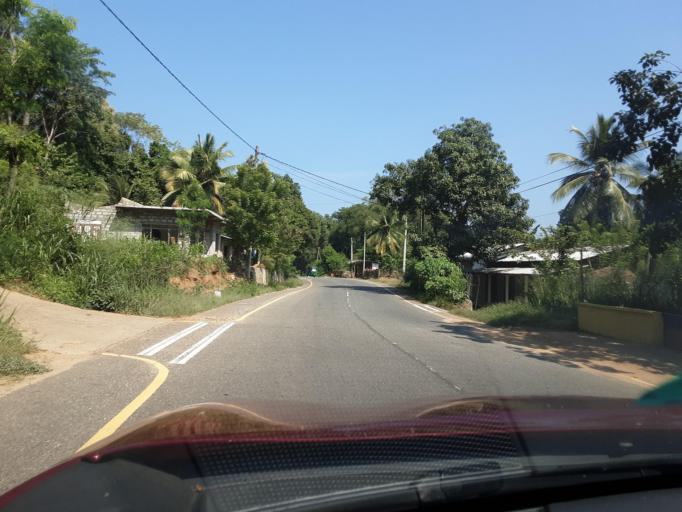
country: LK
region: Uva
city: Badulla
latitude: 7.1598
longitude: 81.0518
